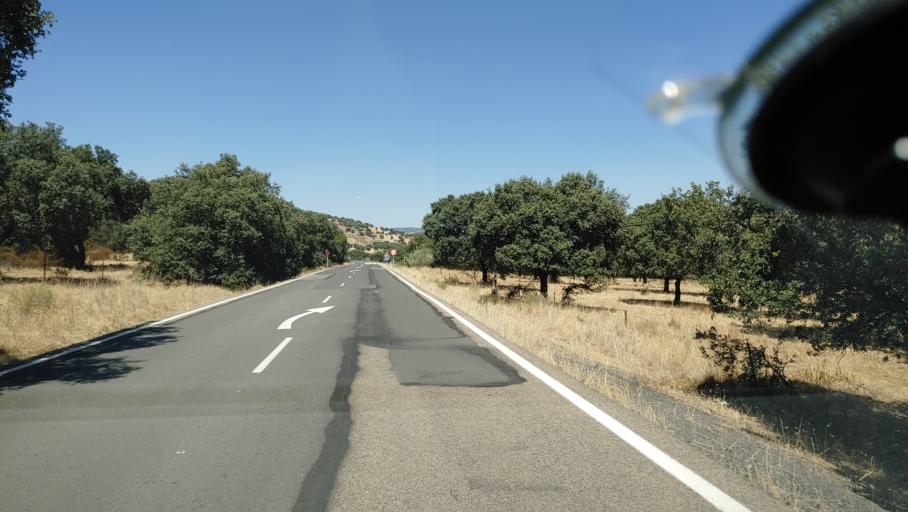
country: ES
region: Castille-La Mancha
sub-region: Provincia de Ciudad Real
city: Alamillo
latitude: 38.7498
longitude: -4.7000
